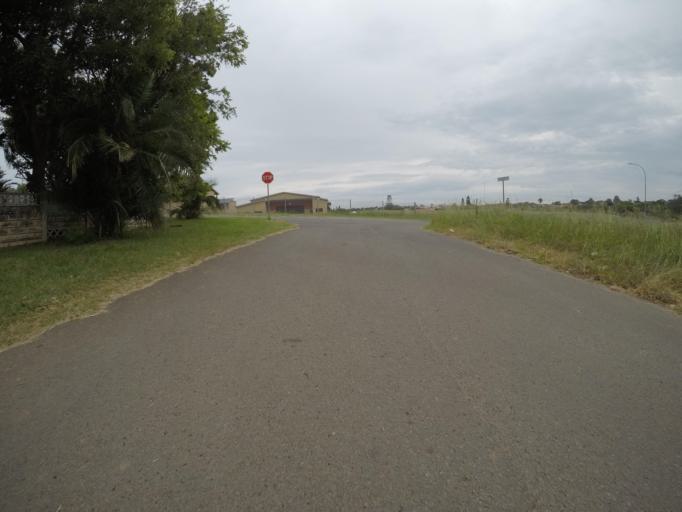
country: ZA
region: Eastern Cape
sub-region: Buffalo City Metropolitan Municipality
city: East London
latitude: -32.9985
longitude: 27.8576
